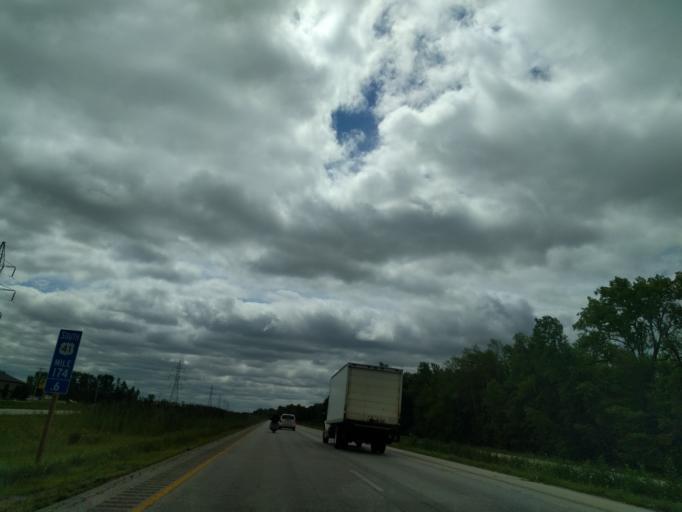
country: US
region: Wisconsin
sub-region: Brown County
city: Suamico
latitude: 44.6088
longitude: -88.0503
